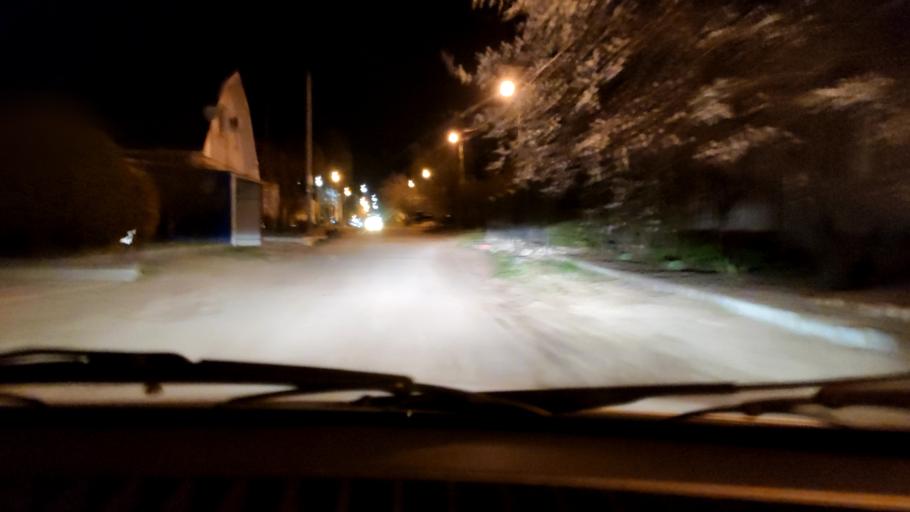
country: RU
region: Voronezj
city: Somovo
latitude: 51.7321
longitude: 39.2666
